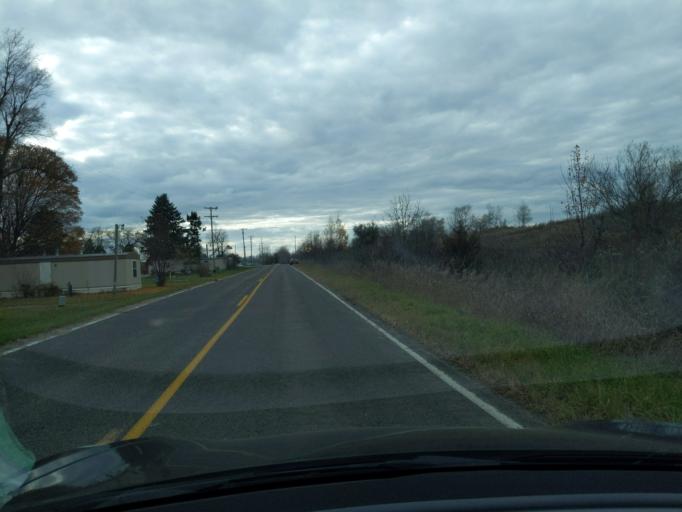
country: US
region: Michigan
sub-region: Ingham County
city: Lansing
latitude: 42.7733
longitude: -84.5387
